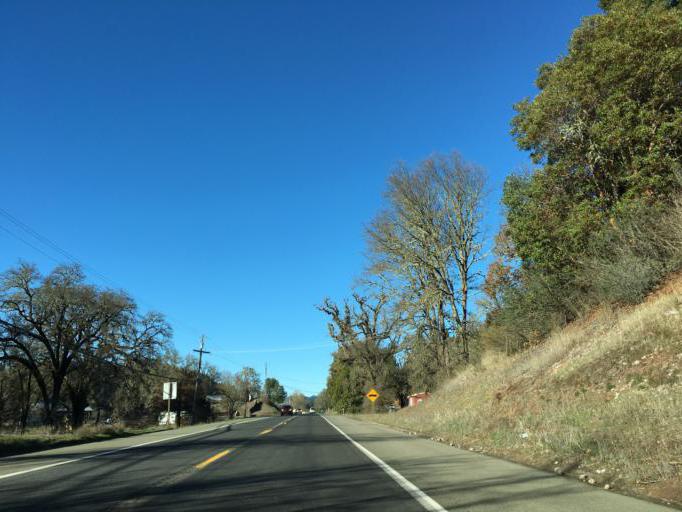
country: US
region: California
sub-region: Mendocino County
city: Laytonville
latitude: 39.6989
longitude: -123.4859
